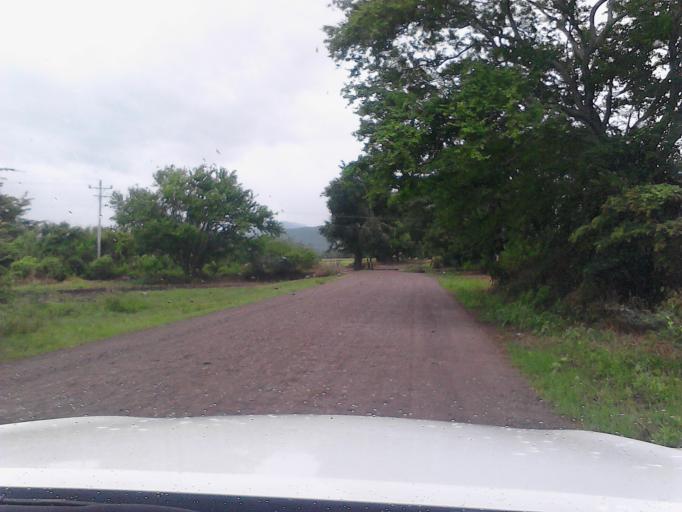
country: NI
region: Matagalpa
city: Ciudad Dario
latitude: 12.8990
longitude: -86.1447
